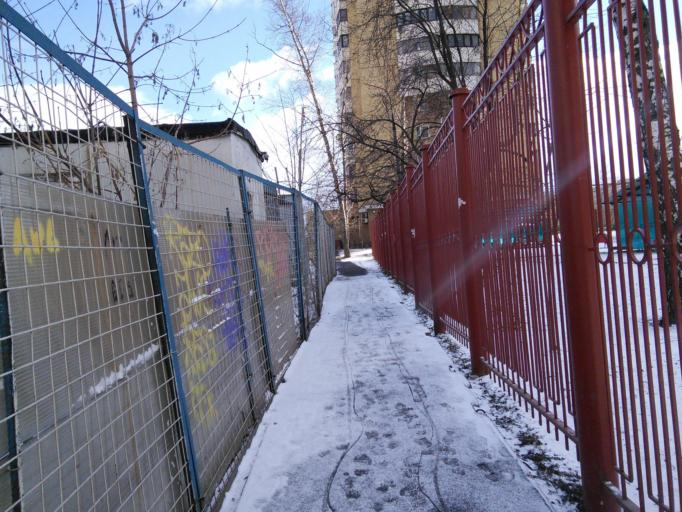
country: RU
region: Moscow
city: Davydkovo
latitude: 55.7316
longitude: 37.4677
